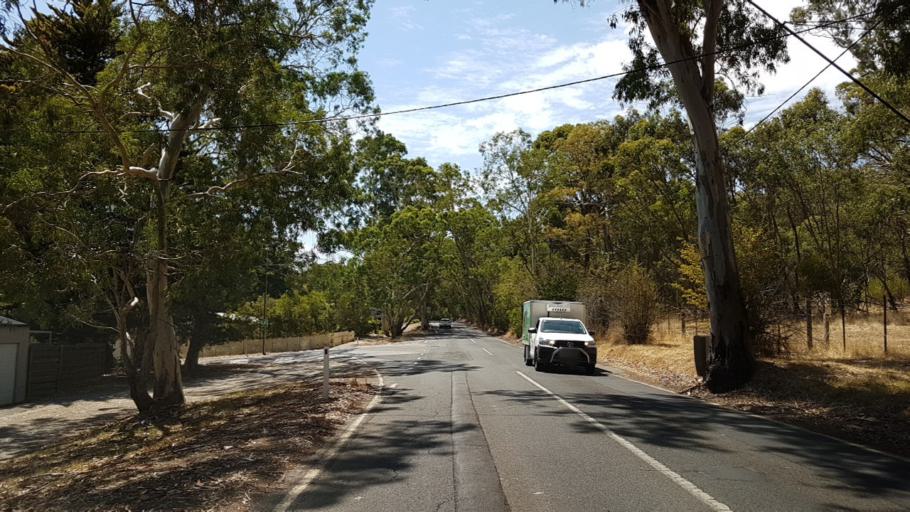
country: AU
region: South Australia
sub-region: Mitcham
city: Belair
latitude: -35.0064
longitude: 138.6330
